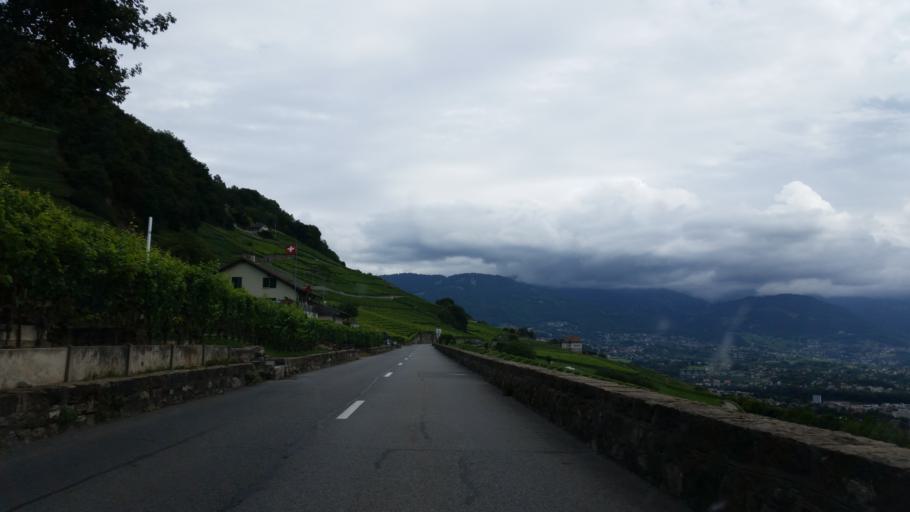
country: CH
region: Vaud
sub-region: Riviera-Pays-d'Enhaut District
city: Chardonne
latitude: 46.4760
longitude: 6.8122
